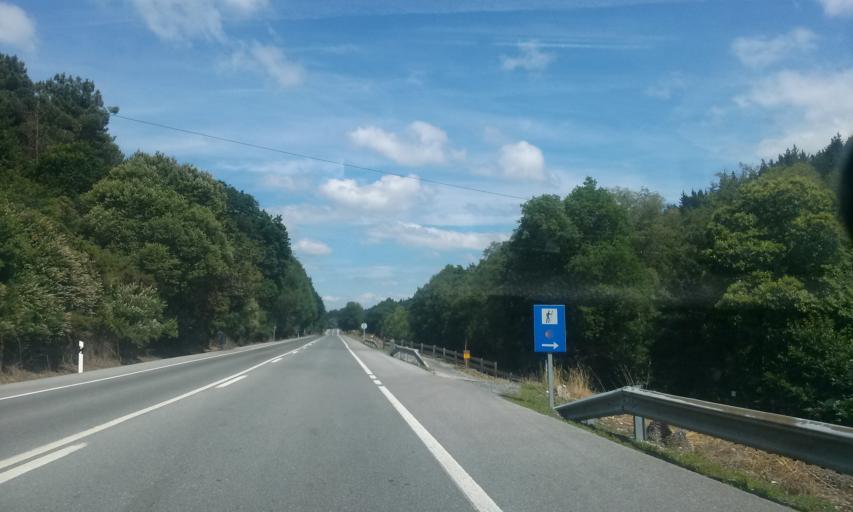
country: ES
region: Galicia
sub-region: Provincia de Lugo
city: Guitiriz
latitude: 43.1726
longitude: -7.7935
